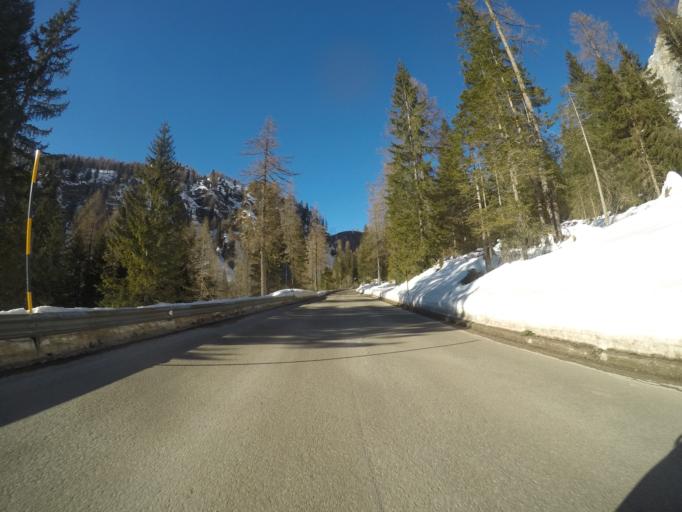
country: IT
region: Veneto
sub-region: Provincia di Belluno
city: Falcade Alto
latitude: 46.2792
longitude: 11.8000
